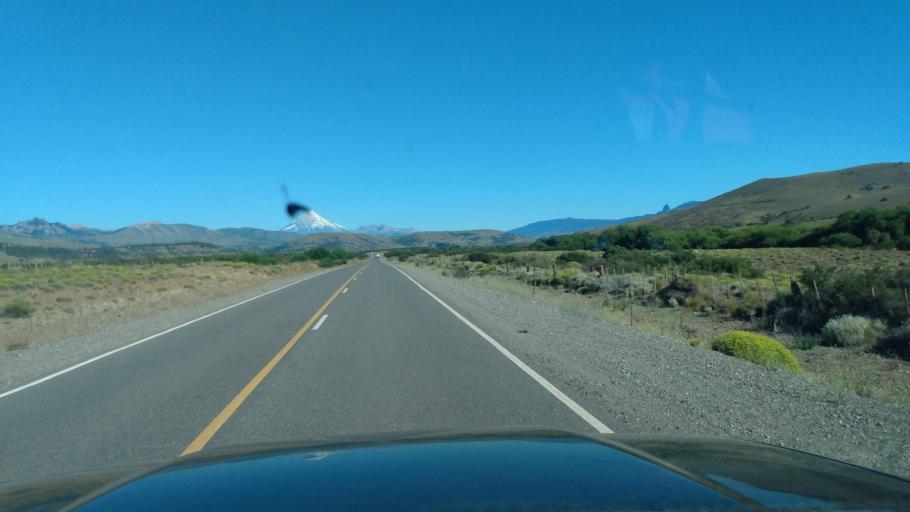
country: AR
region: Neuquen
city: Junin de los Andes
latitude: -39.8904
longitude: -71.1522
